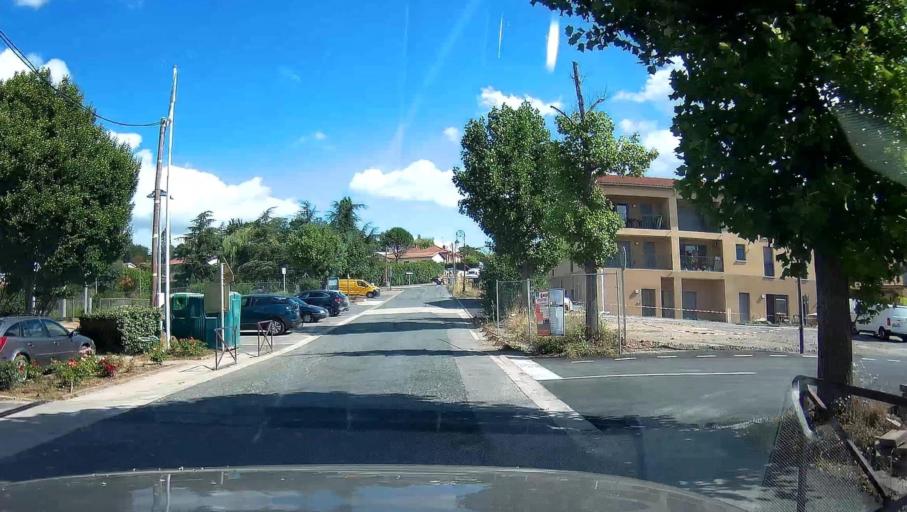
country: FR
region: Rhone-Alpes
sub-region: Departement du Rhone
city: Liergues
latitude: 45.9711
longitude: 4.6640
